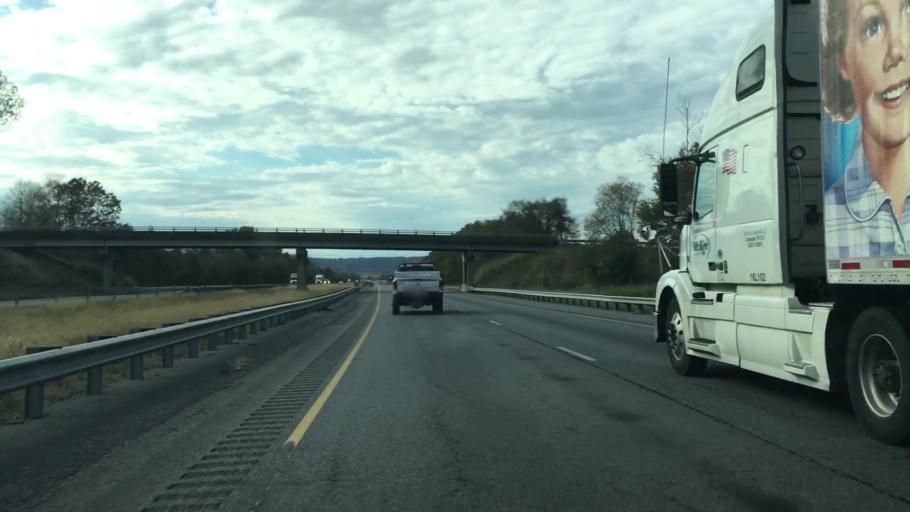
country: US
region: Arkansas
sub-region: Pope County
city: Atkins
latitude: 35.2475
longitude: -92.8711
